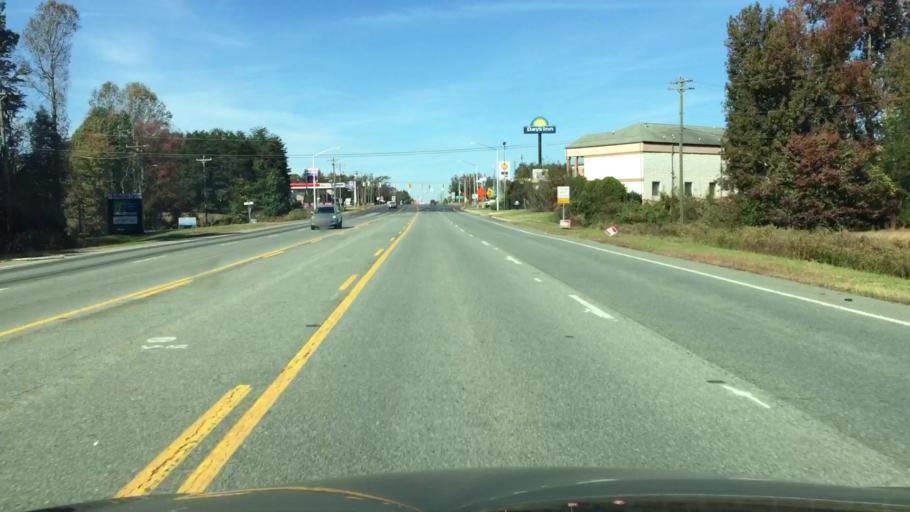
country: US
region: North Carolina
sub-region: Rockingham County
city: Reidsville
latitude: 36.3242
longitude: -79.6383
